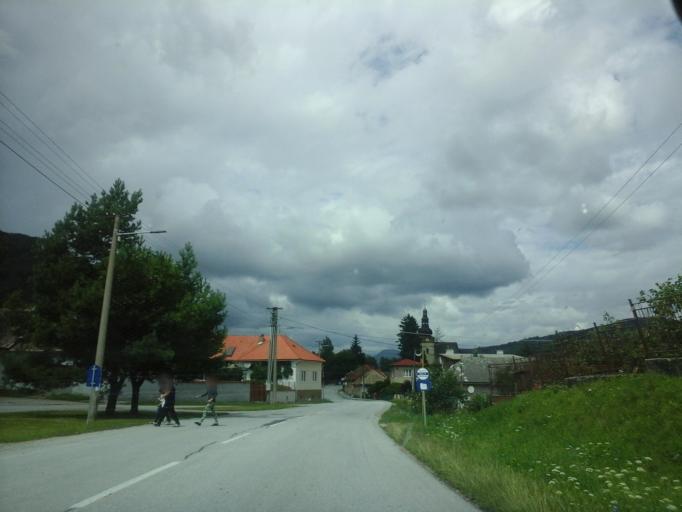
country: SK
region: Kosicky
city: Dobsina
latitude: 48.6544
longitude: 20.3655
